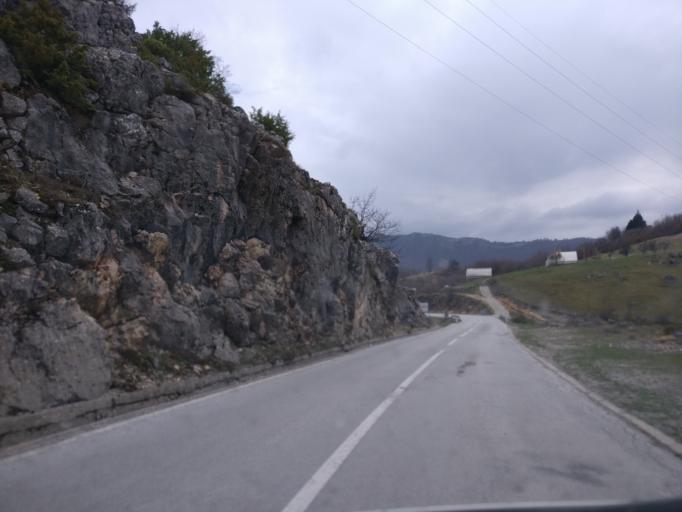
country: ME
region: Opstina Pluzine
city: Pluzine
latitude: 43.1187
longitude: 18.8184
